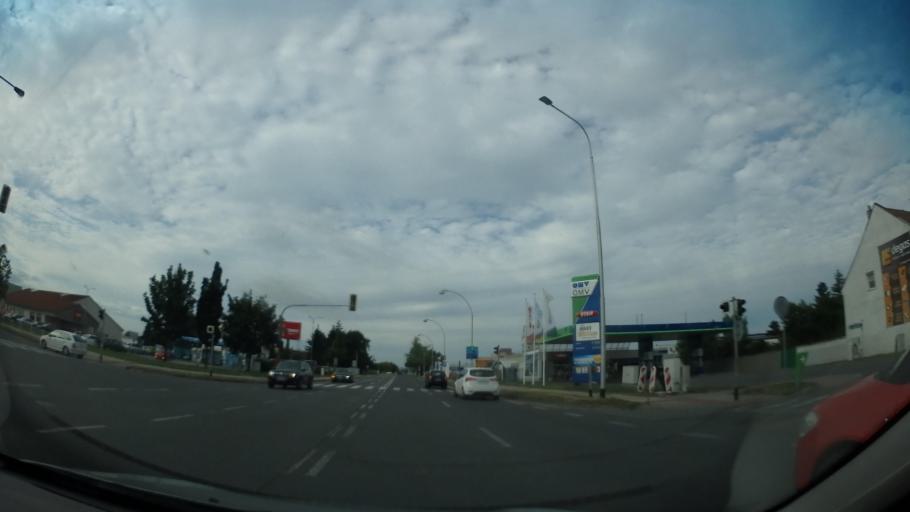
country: CZ
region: Zlin
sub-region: Okres Kromeriz
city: Kromeriz
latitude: 49.3060
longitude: 17.4048
